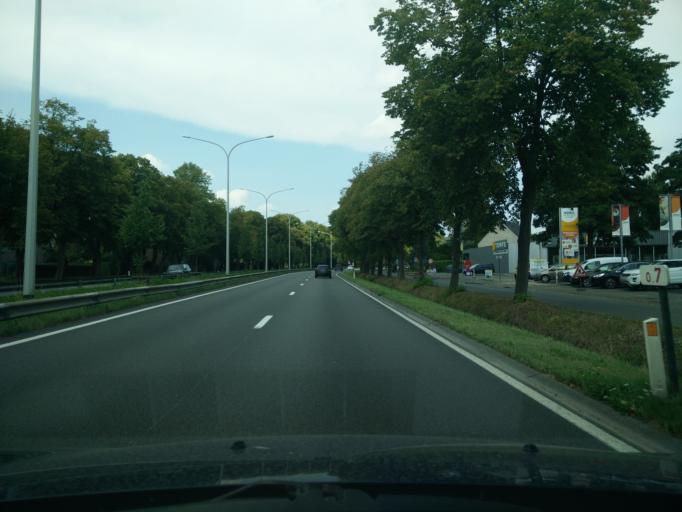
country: BE
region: Flanders
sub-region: Provincie Oost-Vlaanderen
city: Aalst
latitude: 50.9225
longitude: 4.0315
